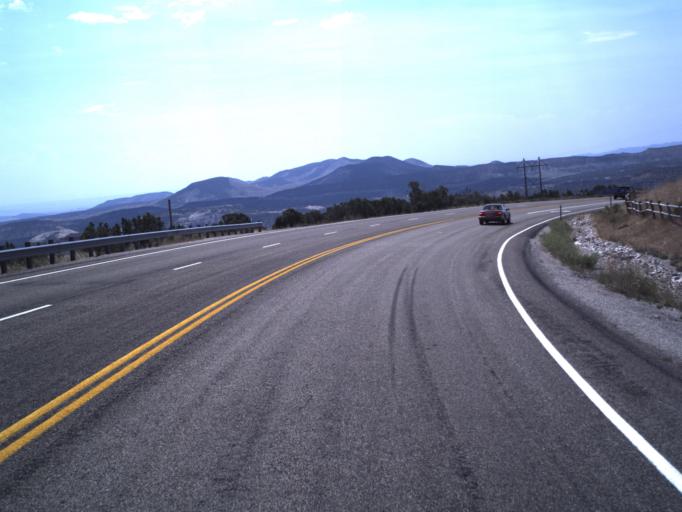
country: US
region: Utah
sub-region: Uintah County
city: Vernal
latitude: 40.6233
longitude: -109.4732
